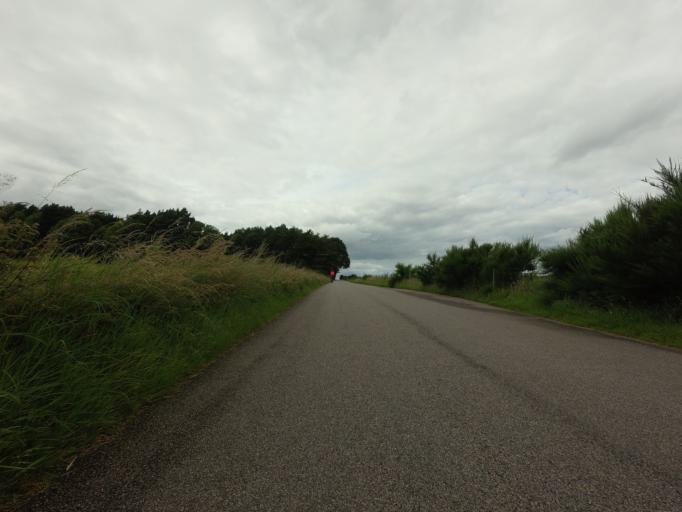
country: GB
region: Scotland
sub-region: Moray
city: Forres
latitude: 57.6015
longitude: -3.7236
